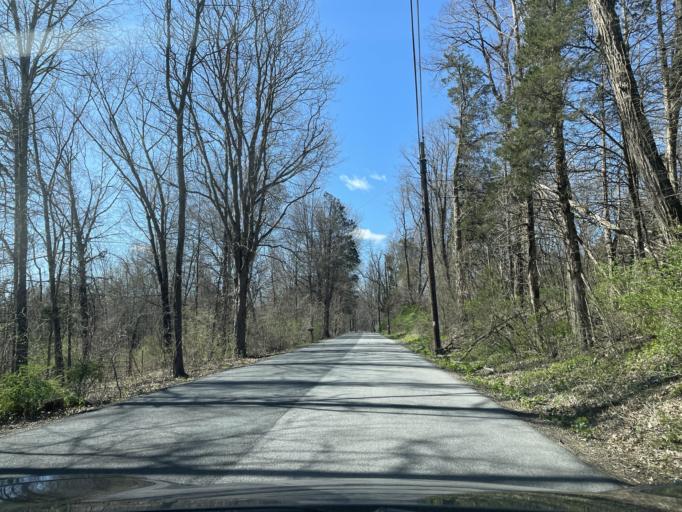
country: US
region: New York
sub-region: Ulster County
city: Saugerties South
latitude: 42.0538
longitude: -73.9912
